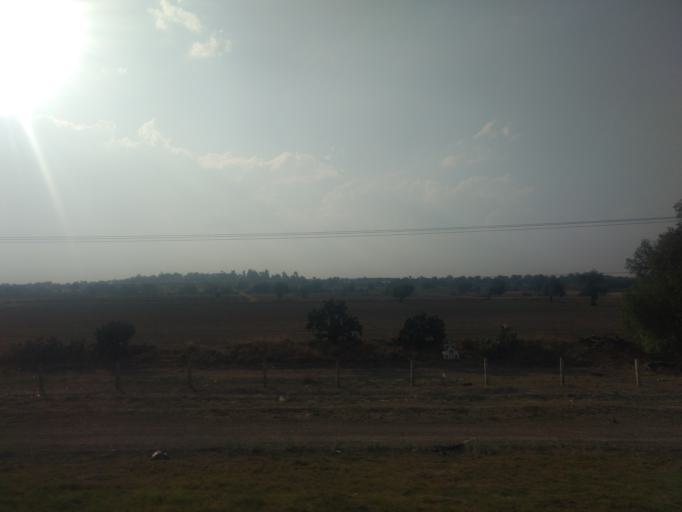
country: MX
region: Morelos
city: Nopaltepec
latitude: 19.7746
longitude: -98.7414
